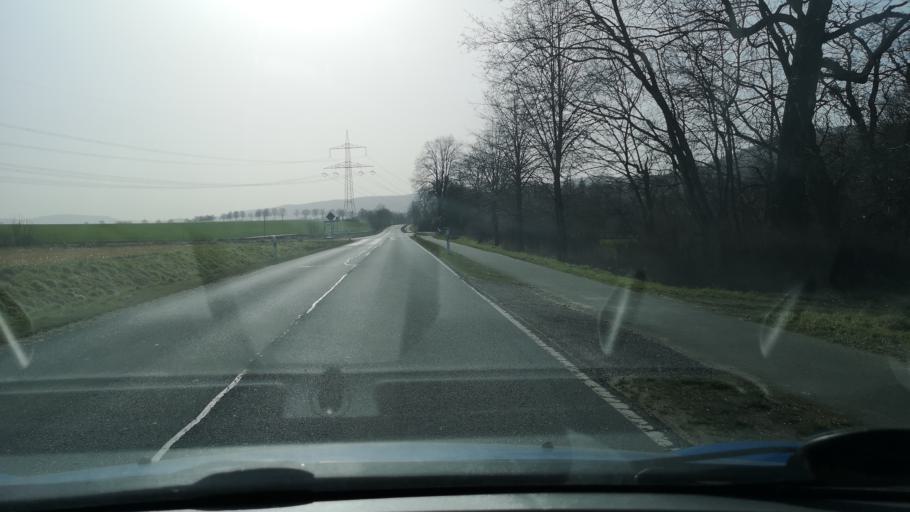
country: DE
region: Lower Saxony
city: Salzhemmendorf
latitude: 52.0507
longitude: 9.5955
